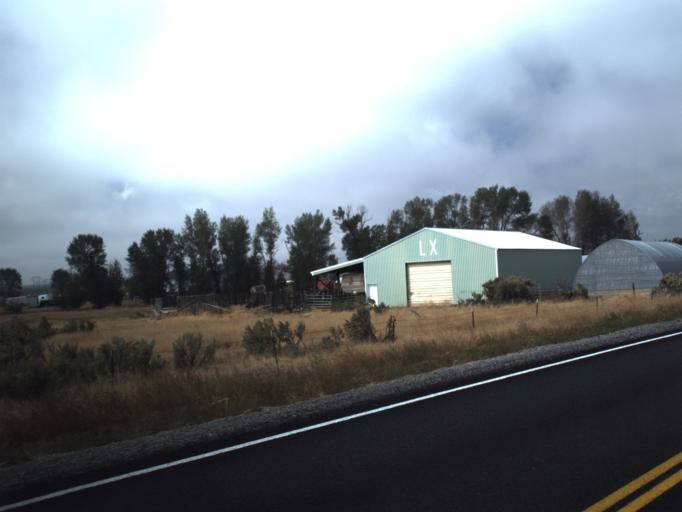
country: US
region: Utah
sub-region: Rich County
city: Randolph
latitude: 41.5174
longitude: -111.1607
